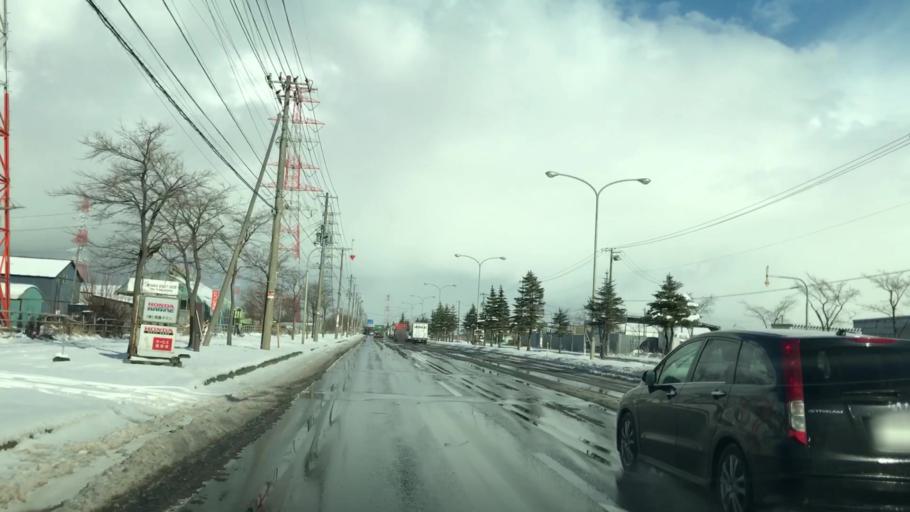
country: JP
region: Hokkaido
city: Sapporo
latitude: 43.1466
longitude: 141.4120
